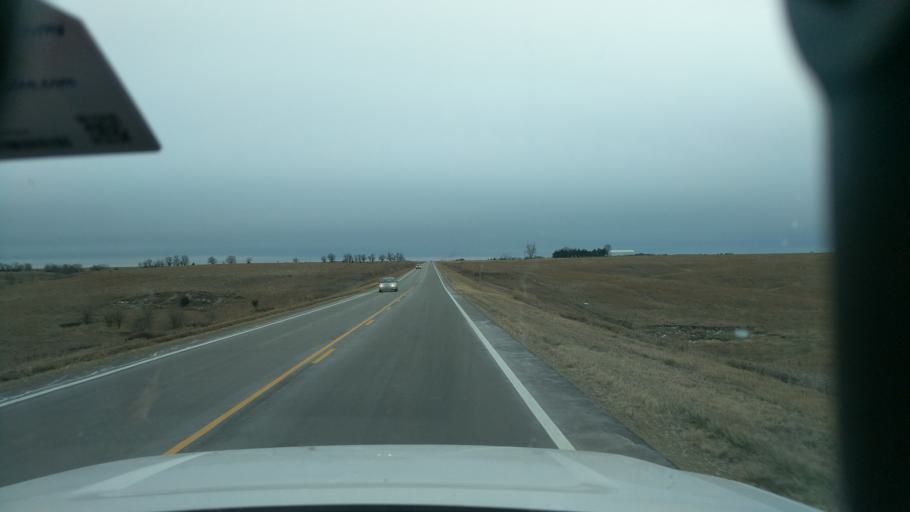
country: US
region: Kansas
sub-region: Dickinson County
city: Herington
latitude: 38.7817
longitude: -96.9273
